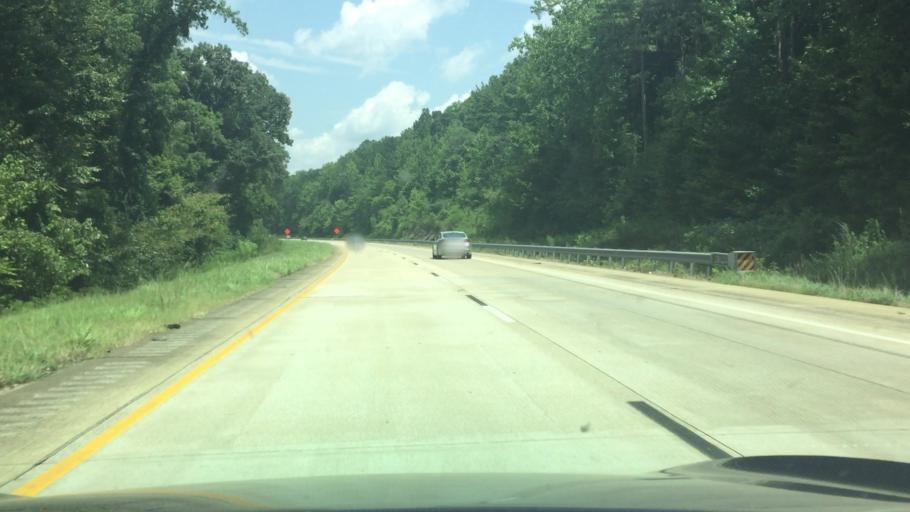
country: US
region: Alabama
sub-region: Etowah County
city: Gadsden
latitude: 34.0525
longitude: -86.0432
